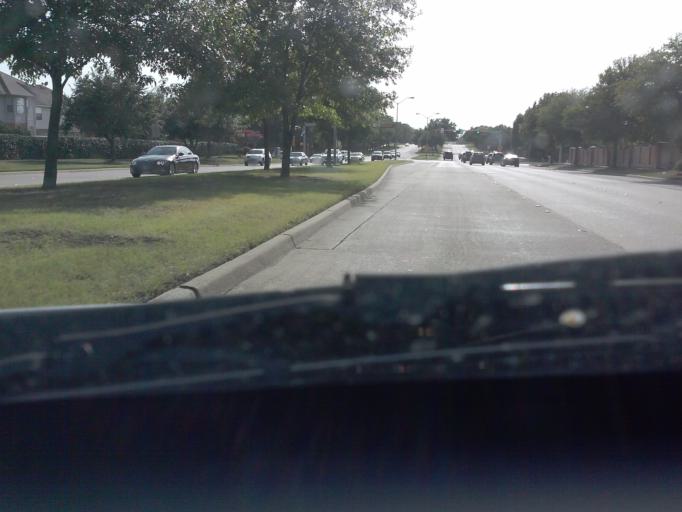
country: US
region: Texas
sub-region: Collin County
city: Plano
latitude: 33.0564
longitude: -96.7789
